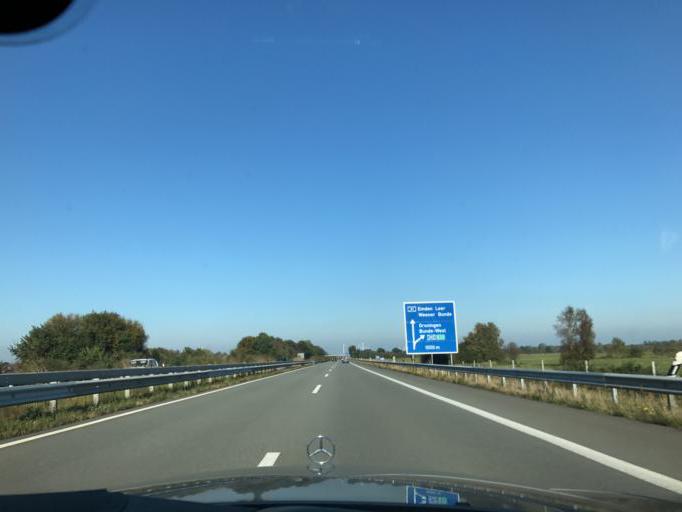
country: DE
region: Lower Saxony
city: Bunde
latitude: 53.1532
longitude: 7.2794
